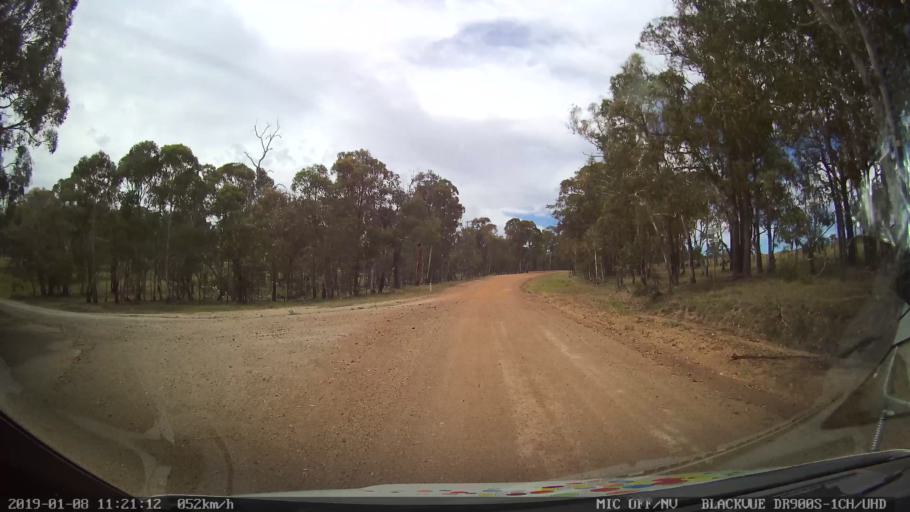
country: AU
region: New South Wales
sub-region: Guyra
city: Guyra
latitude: -30.2356
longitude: 151.5657
